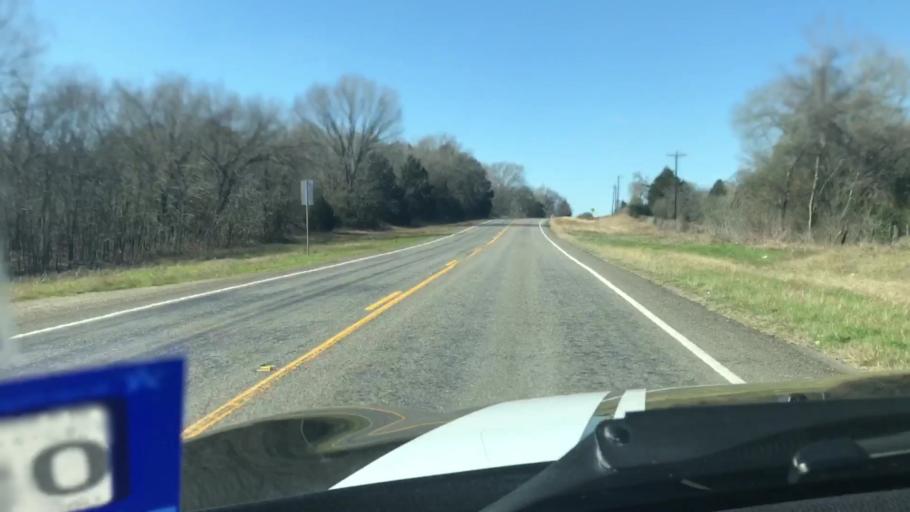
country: US
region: Texas
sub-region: Robertson County
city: Calvert
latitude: 30.8847
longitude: -96.7643
